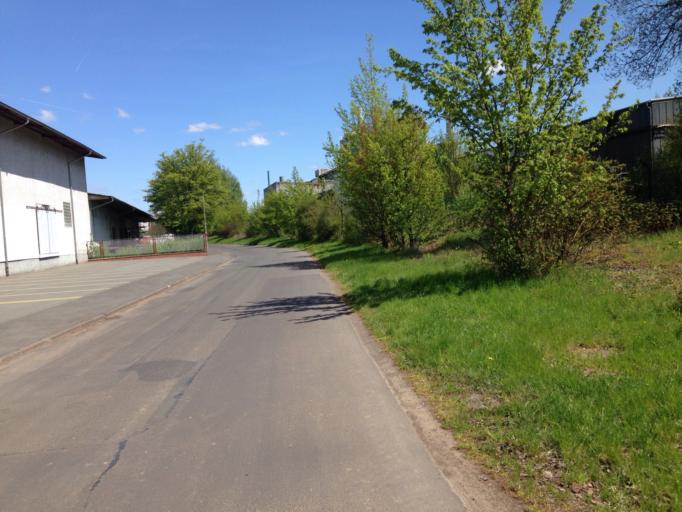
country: DE
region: Hesse
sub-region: Regierungsbezirk Giessen
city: Laubach
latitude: 50.5415
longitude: 8.9771
